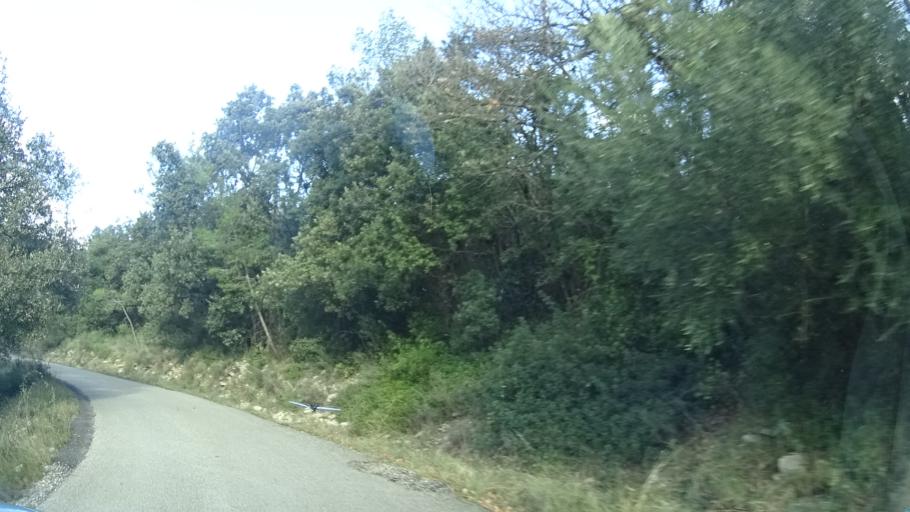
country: FR
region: Languedoc-Roussillon
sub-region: Departement de l'Herault
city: Claret
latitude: 43.8443
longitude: 3.8827
